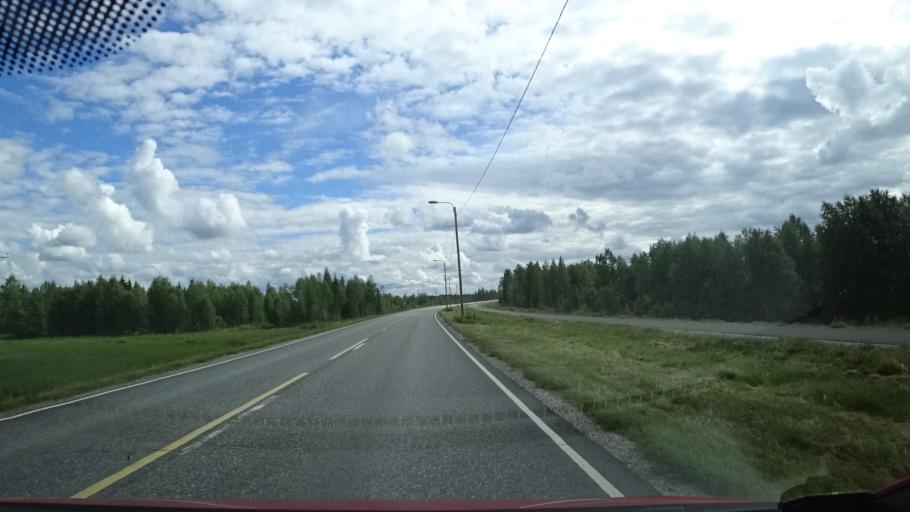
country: FI
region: Lapland
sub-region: Tunturi-Lappi
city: Kittilae
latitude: 67.4840
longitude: 24.9186
